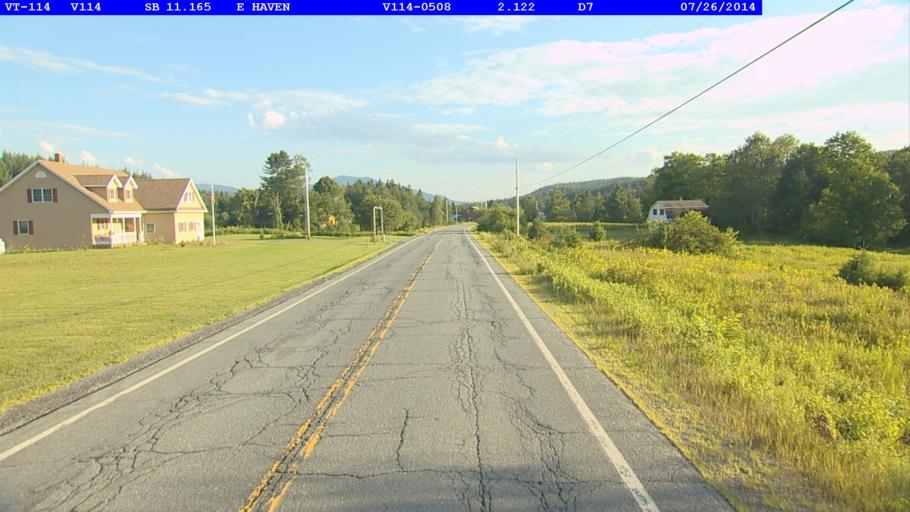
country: US
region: Vermont
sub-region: Caledonia County
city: Lyndonville
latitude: 44.6686
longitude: -71.8865
